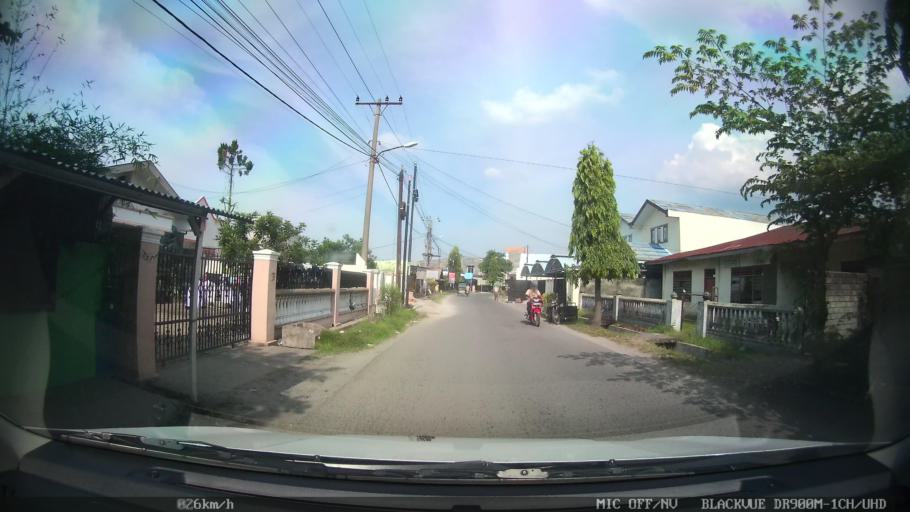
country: ID
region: North Sumatra
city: Binjai
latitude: 3.6109
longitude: 98.4961
